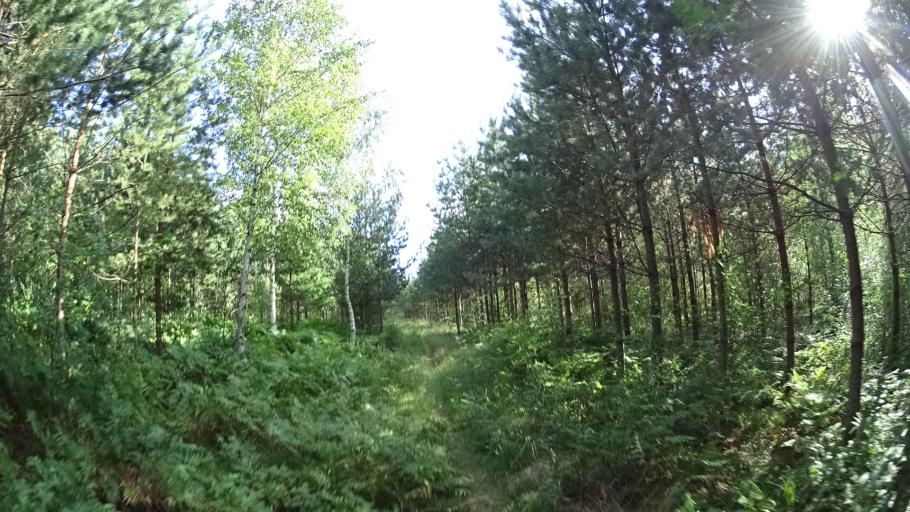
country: FI
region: Uusimaa
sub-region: Helsinki
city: Vihti
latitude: 60.3702
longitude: 24.3659
